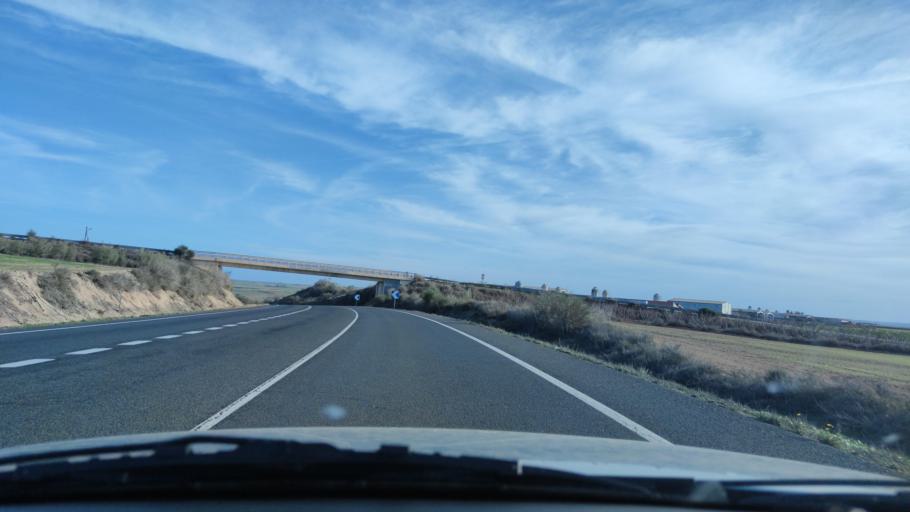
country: ES
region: Catalonia
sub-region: Provincia de Lleida
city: Alfes
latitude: 41.5186
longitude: 0.6253
